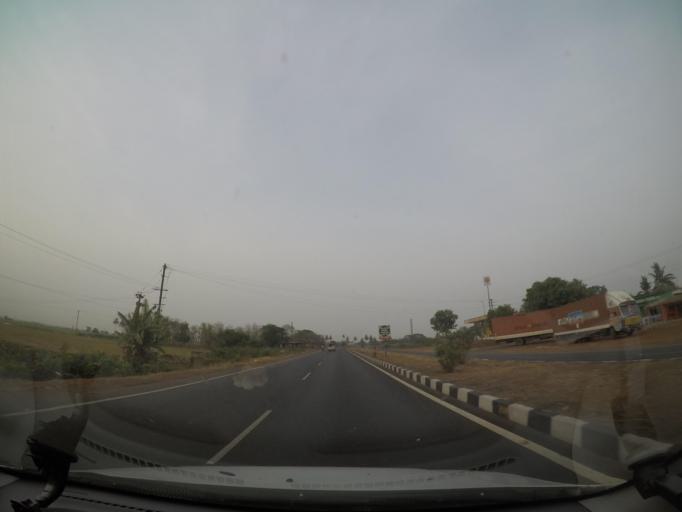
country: IN
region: Andhra Pradesh
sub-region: Krishna
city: Gannavaram
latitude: 16.6131
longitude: 80.9233
